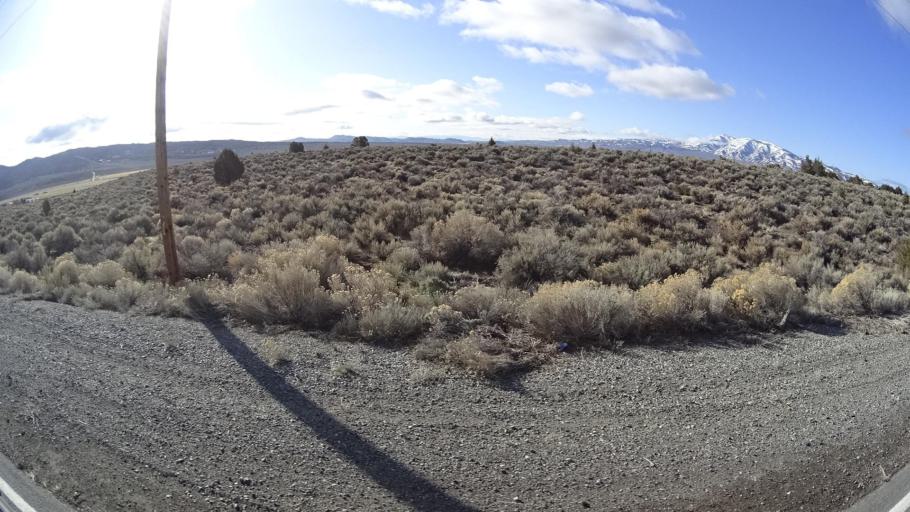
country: US
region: Nevada
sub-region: Washoe County
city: Cold Springs
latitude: 39.7161
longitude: -119.8939
